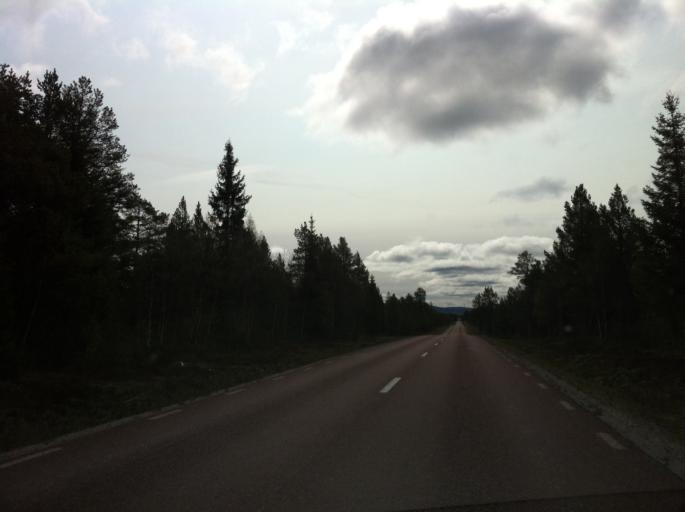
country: NO
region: Hedmark
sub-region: Engerdal
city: Engerdal
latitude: 62.4874
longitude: 12.6496
